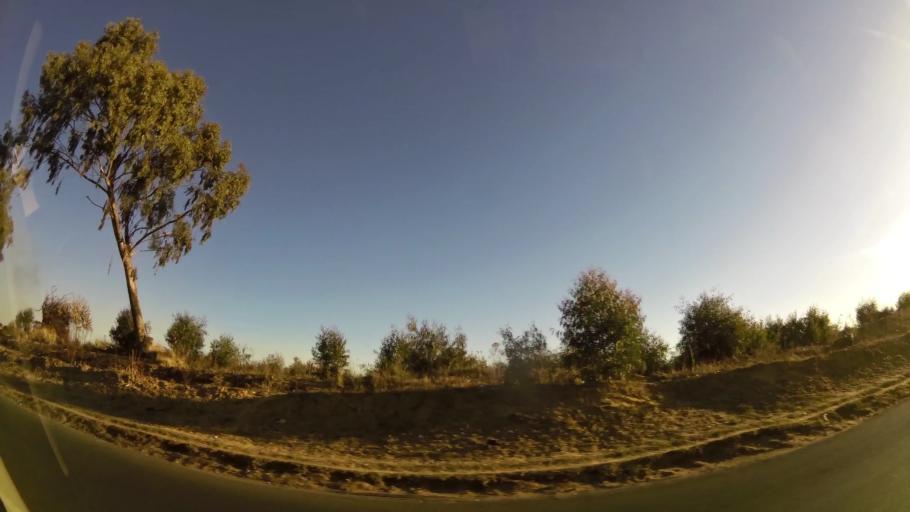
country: ZA
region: Gauteng
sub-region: City of Johannesburg Metropolitan Municipality
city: Roodepoort
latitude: -26.1749
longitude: 27.8905
